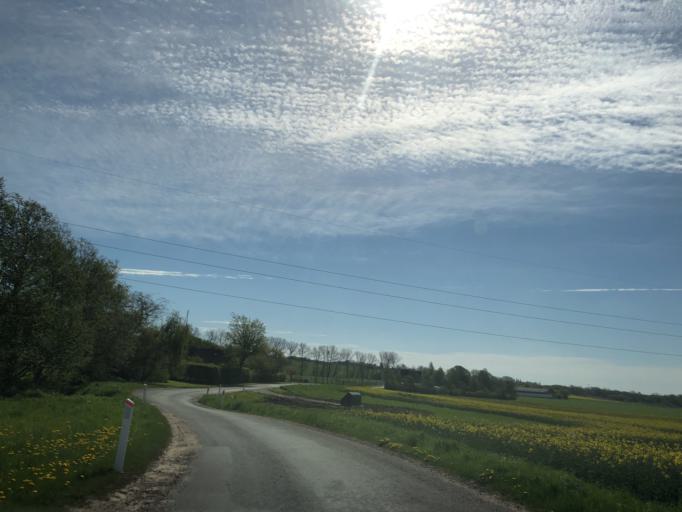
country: DK
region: Zealand
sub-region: Slagelse Kommune
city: Forlev
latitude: 55.3837
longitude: 11.2875
